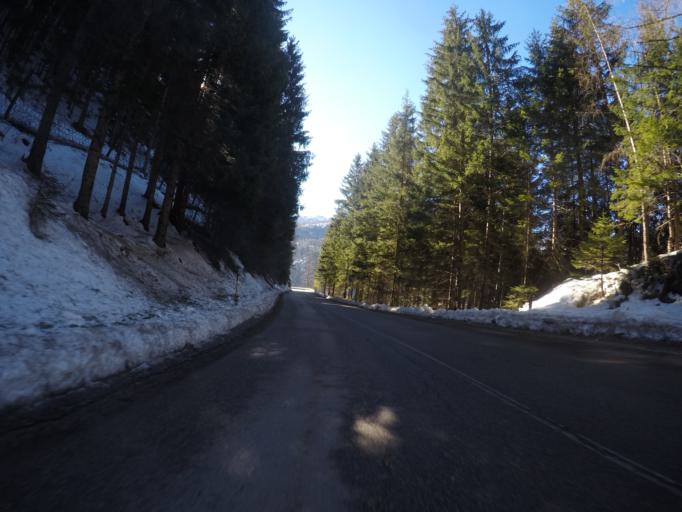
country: IT
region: Veneto
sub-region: Provincia di Belluno
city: Colle Santa Lucia
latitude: 46.4457
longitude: 11.9946
